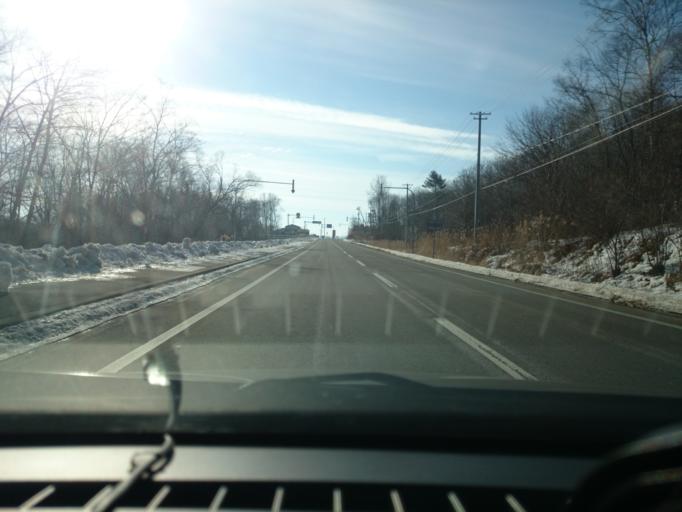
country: JP
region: Hokkaido
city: Otofuke
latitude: 43.2533
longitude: 143.5660
